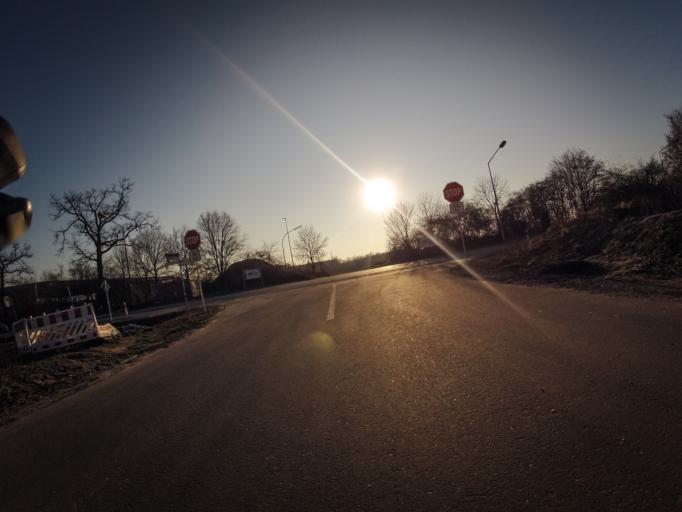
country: DE
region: Lower Saxony
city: Wallenhorst
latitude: 52.3106
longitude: 8.0158
